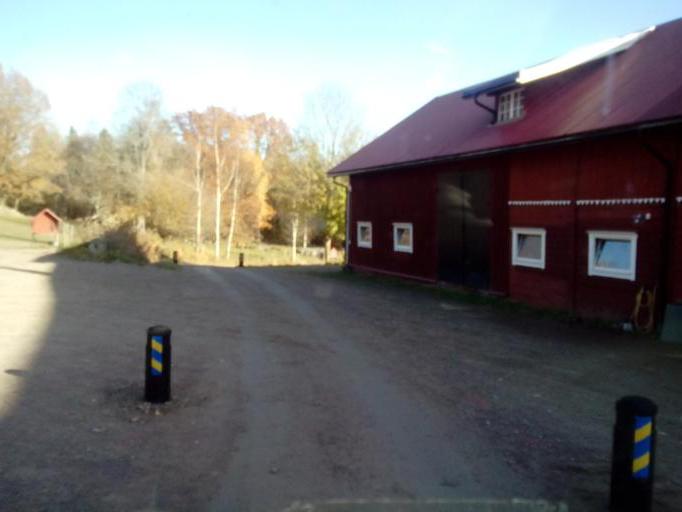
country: SE
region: Kalmar
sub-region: Vimmerby Kommun
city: Vimmerby
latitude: 57.6857
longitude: 15.9078
